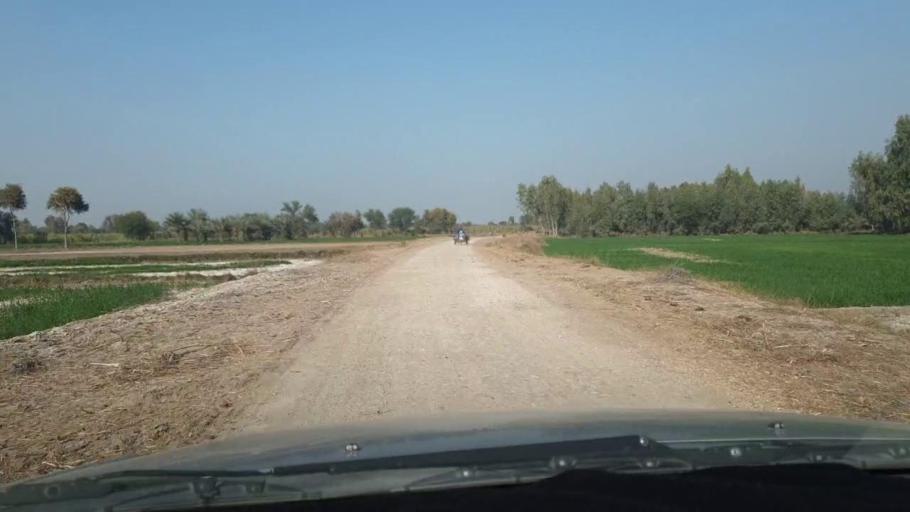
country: PK
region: Sindh
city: Mirpur Mathelo
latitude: 27.9182
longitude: 69.5566
